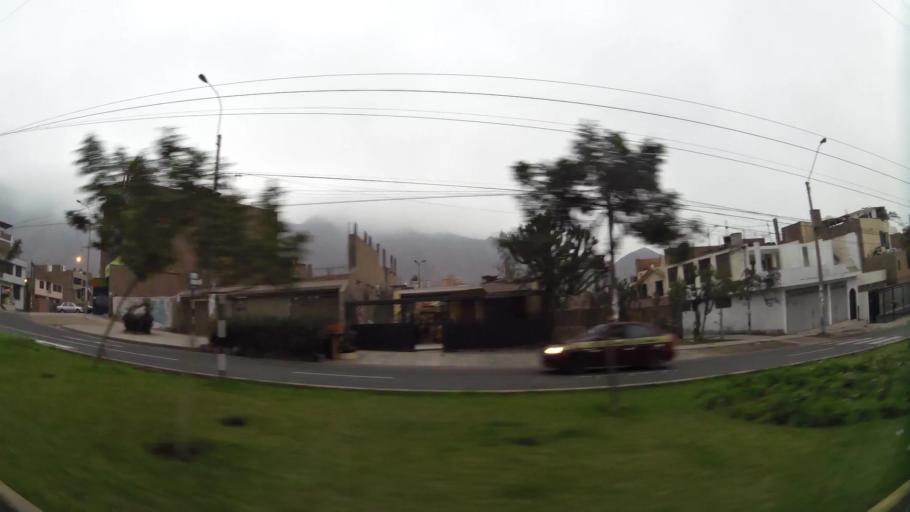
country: PE
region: Lima
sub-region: Lima
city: La Molina
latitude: -12.1101
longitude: -76.9386
